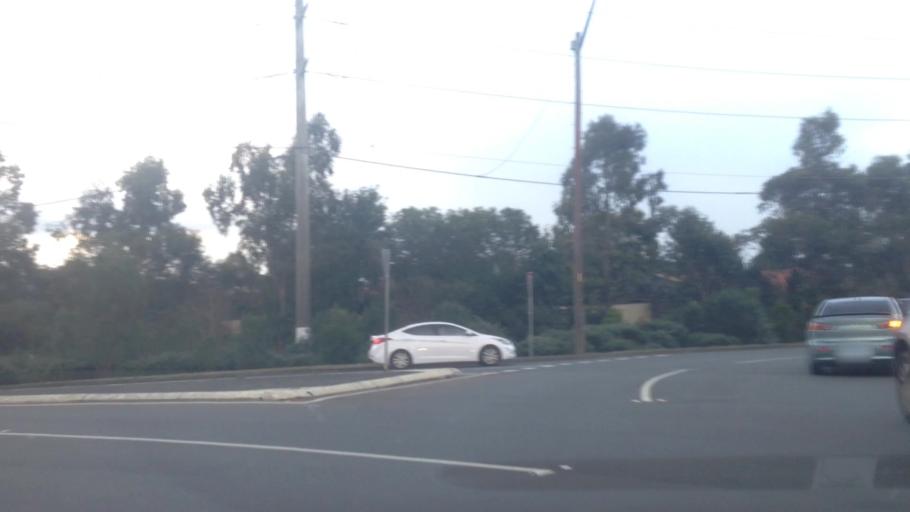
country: AU
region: New South Wales
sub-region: Wyong Shire
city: Kanwal
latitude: -33.2521
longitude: 151.4892
